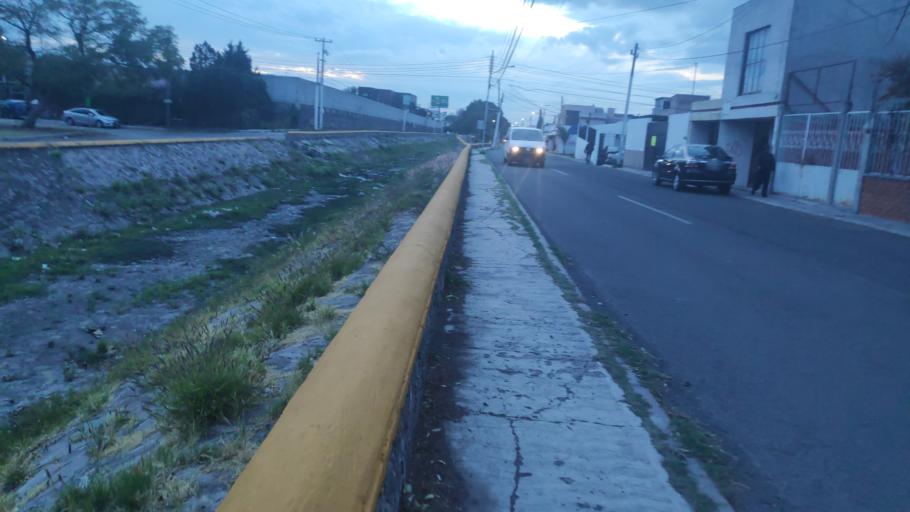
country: MX
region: Queretaro
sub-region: Queretaro
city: Santiago de Queretaro
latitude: 20.5803
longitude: -100.3760
